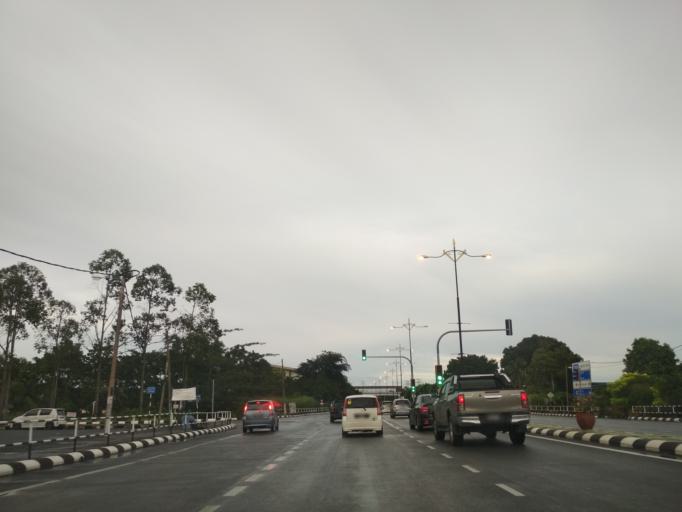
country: MY
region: Perlis
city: Kangar
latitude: 6.4362
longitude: 100.2047
